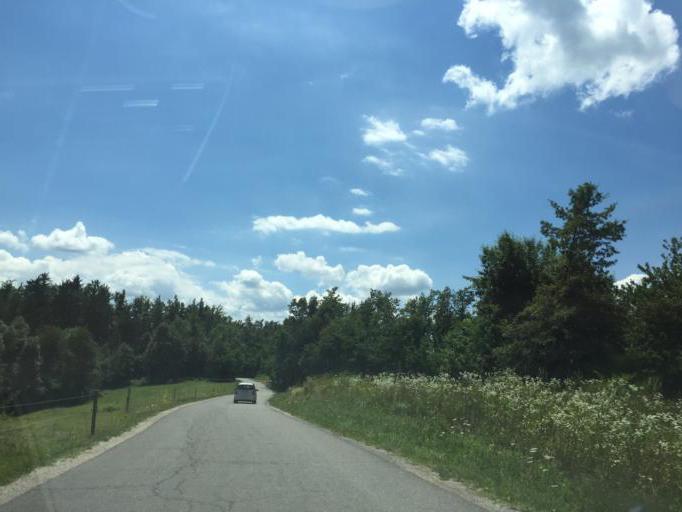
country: SI
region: Postojna
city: Postojna
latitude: 45.8062
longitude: 14.1454
